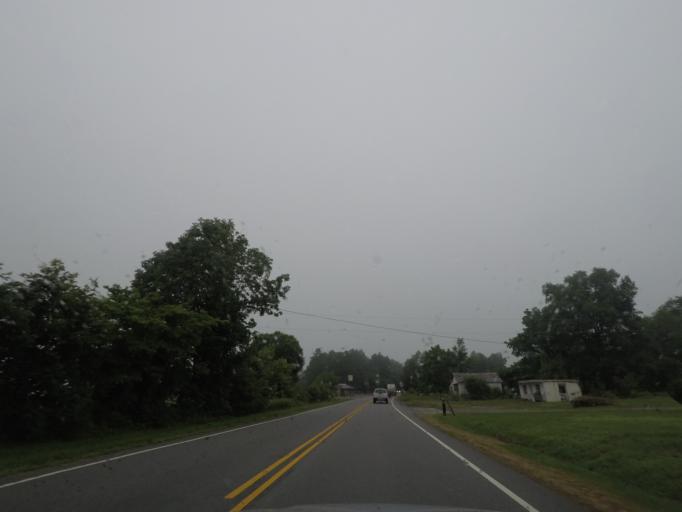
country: US
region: Virginia
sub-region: Prince Edward County
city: Farmville
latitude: 37.3655
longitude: -78.4857
